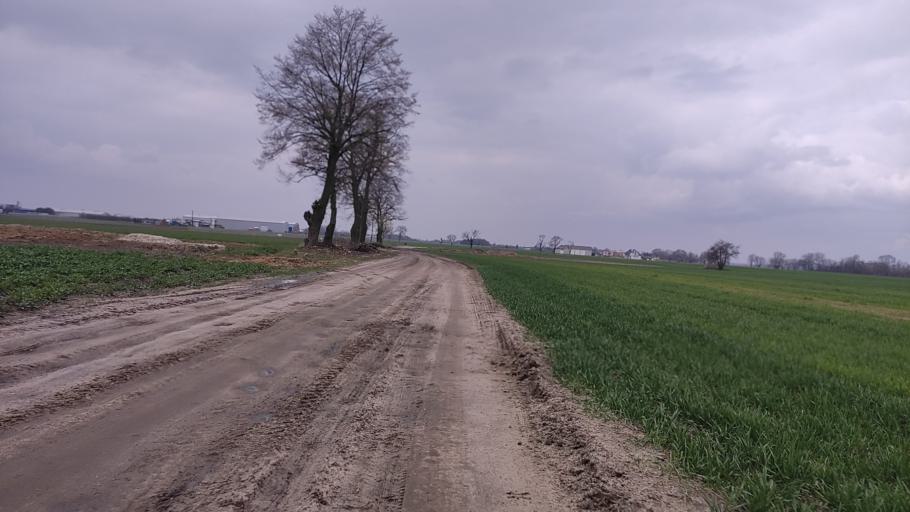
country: PL
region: Greater Poland Voivodeship
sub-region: Powiat poznanski
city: Swarzedz
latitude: 52.4035
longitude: 17.1474
